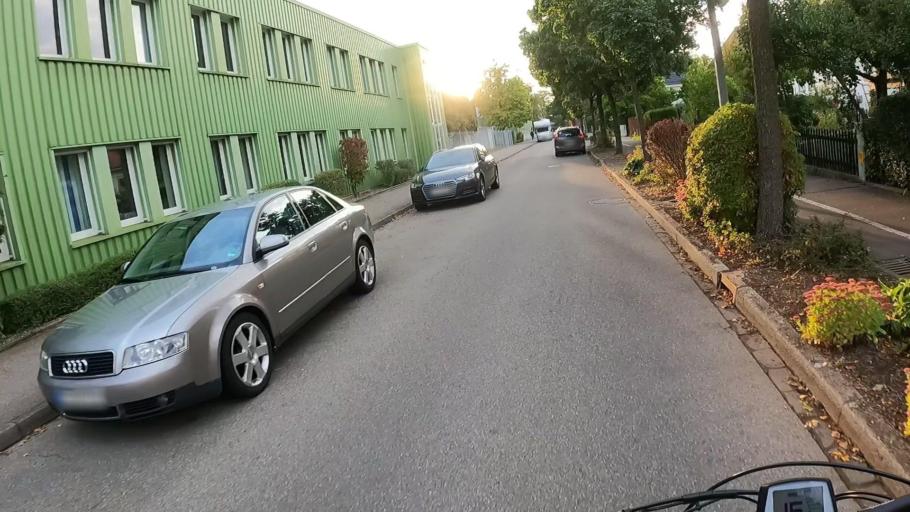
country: DE
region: Baden-Wuerttemberg
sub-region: Freiburg Region
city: Radolfzell am Bodensee
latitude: 47.7426
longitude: 8.9686
